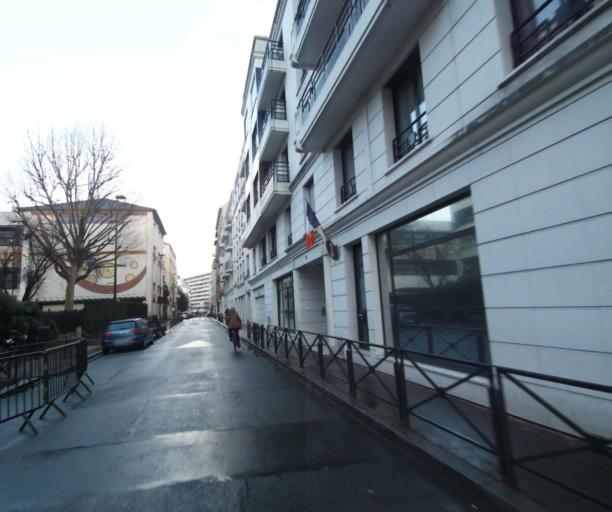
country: FR
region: Ile-de-France
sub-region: Departement des Hauts-de-Seine
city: Levallois-Perret
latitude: 48.8931
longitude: 2.2929
